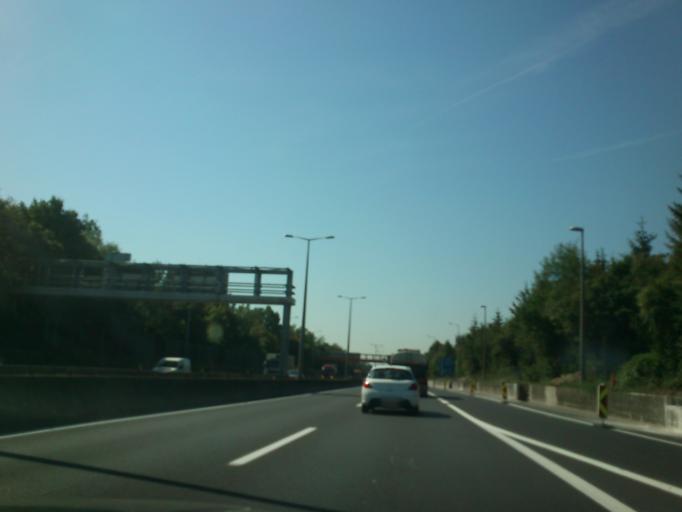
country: AT
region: Upper Austria
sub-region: Politischer Bezirk Linz-Land
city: Leonding
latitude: 48.2587
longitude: 14.2969
